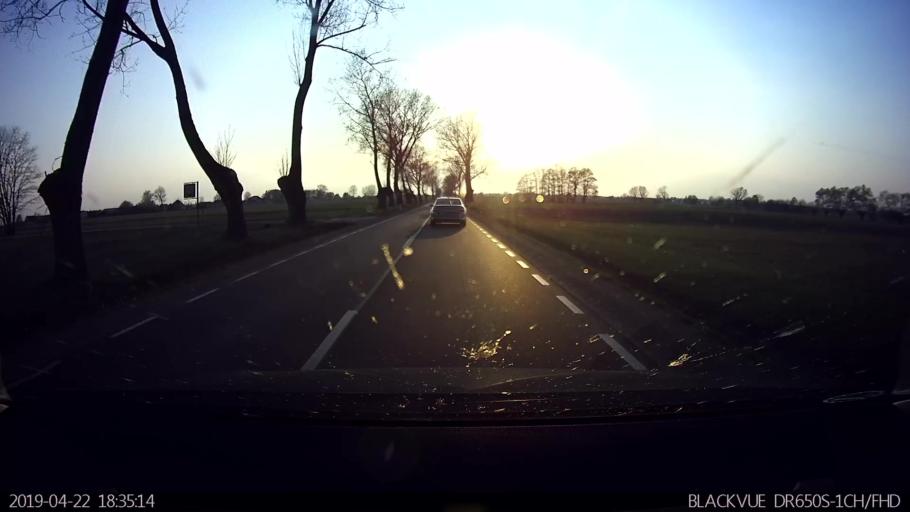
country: PL
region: Masovian Voivodeship
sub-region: Powiat wolominski
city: Klembow
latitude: 52.4455
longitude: 21.3542
